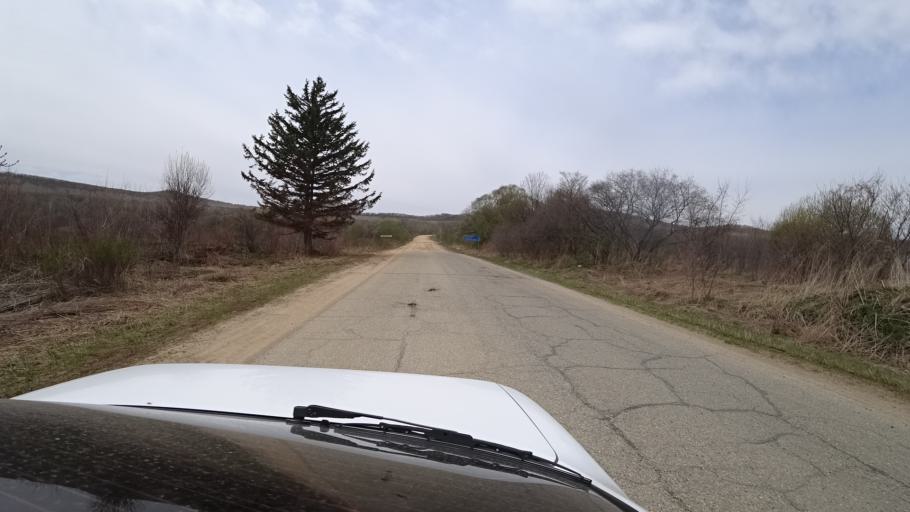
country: RU
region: Primorskiy
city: Dal'nerechensk
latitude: 45.7996
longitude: 134.0995
